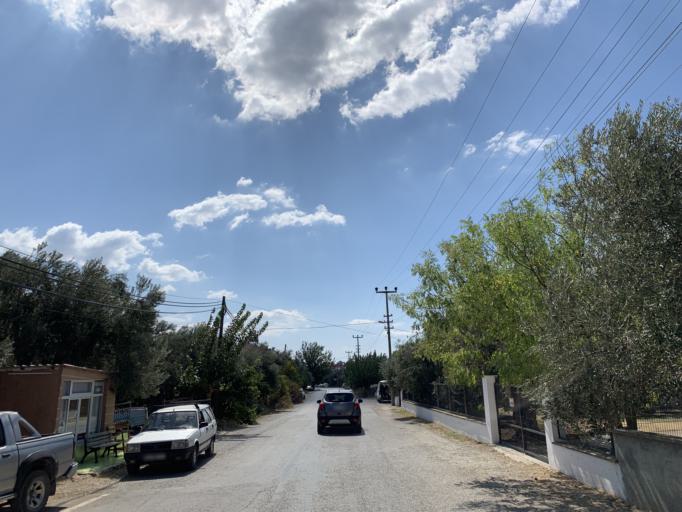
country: TR
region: Balikesir
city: Altinoluk
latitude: 39.5697
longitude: 26.8356
